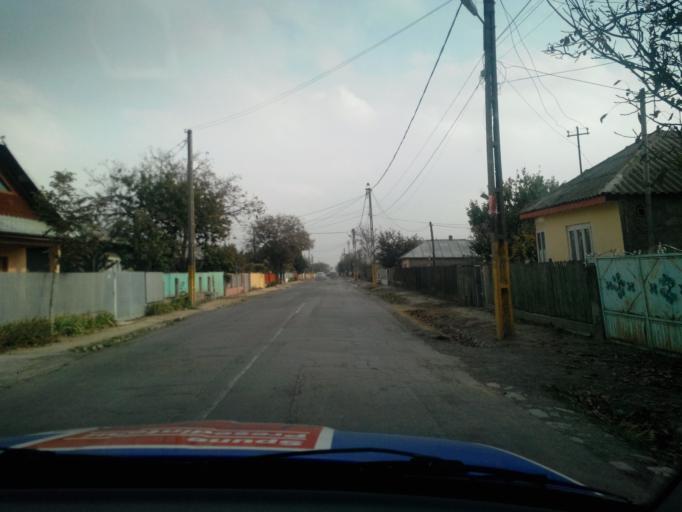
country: RO
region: Galati
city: Galati
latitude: 45.4059
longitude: 28.0536
